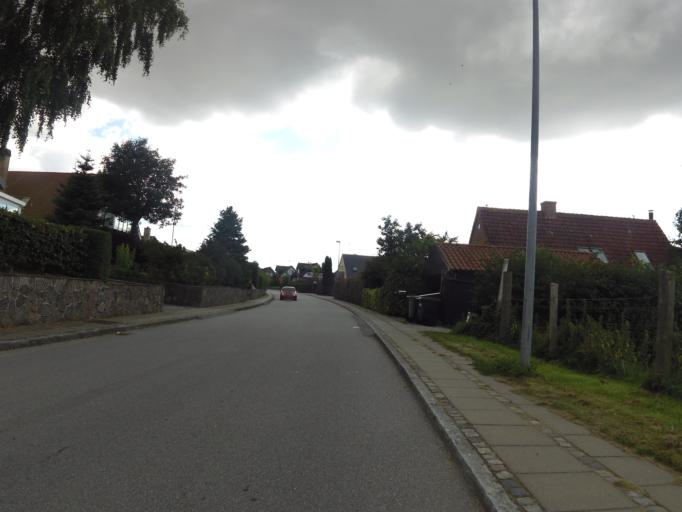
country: DK
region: South Denmark
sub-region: Haderslev Kommune
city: Haderslev
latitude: 55.2435
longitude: 9.4754
